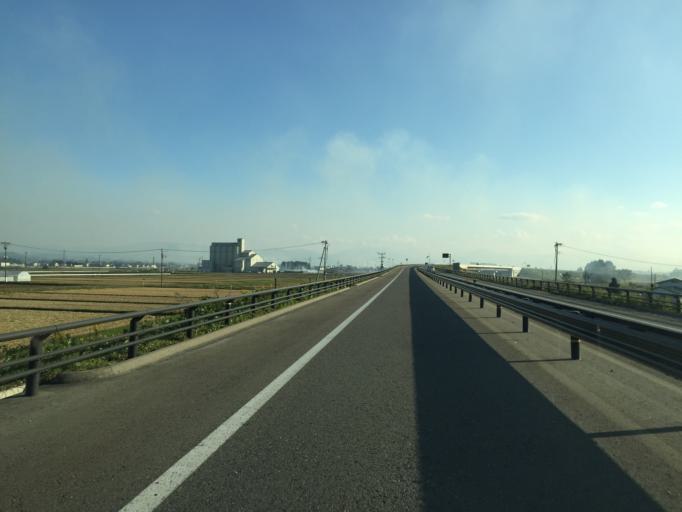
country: JP
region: Fukushima
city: Kitakata
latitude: 37.6169
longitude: 139.8822
